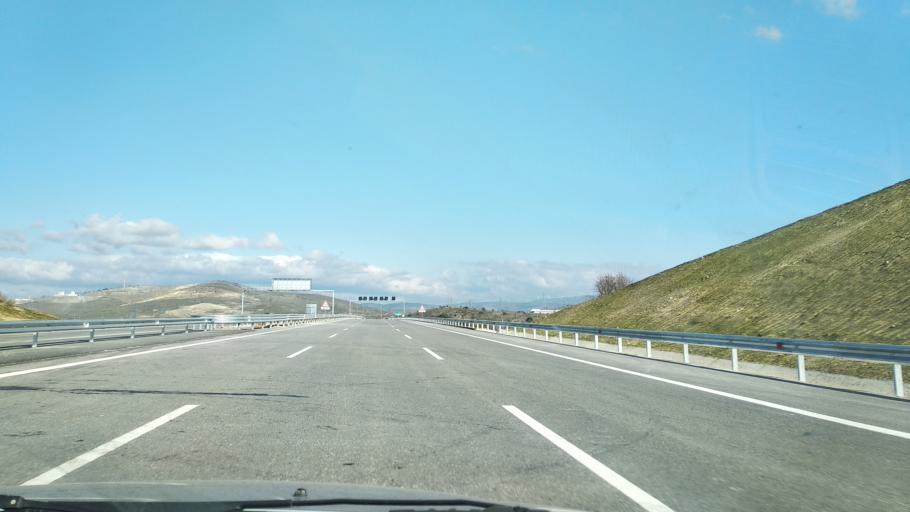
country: TR
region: Izmir
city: Aliaga
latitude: 38.8090
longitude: 27.0208
